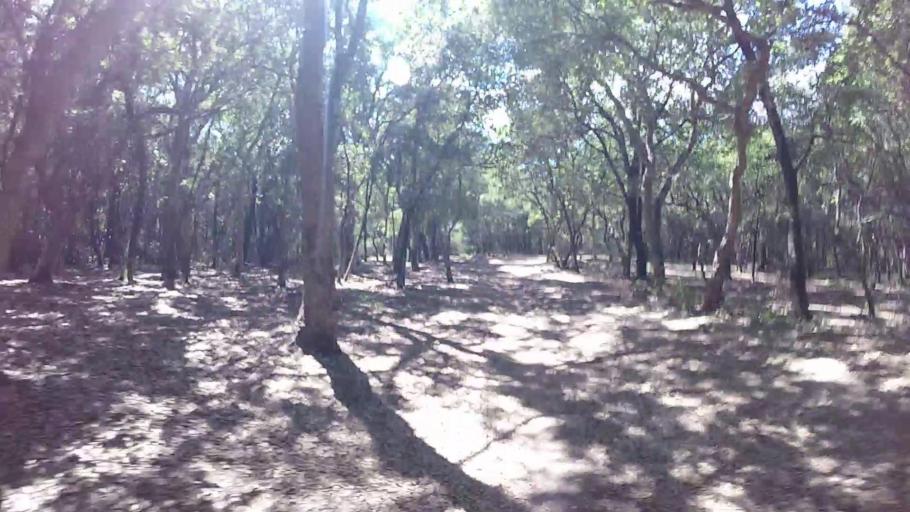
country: FR
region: Provence-Alpes-Cote d'Azur
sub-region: Departement des Alpes-Maritimes
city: Le Cannet
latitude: 43.5965
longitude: 7.0346
